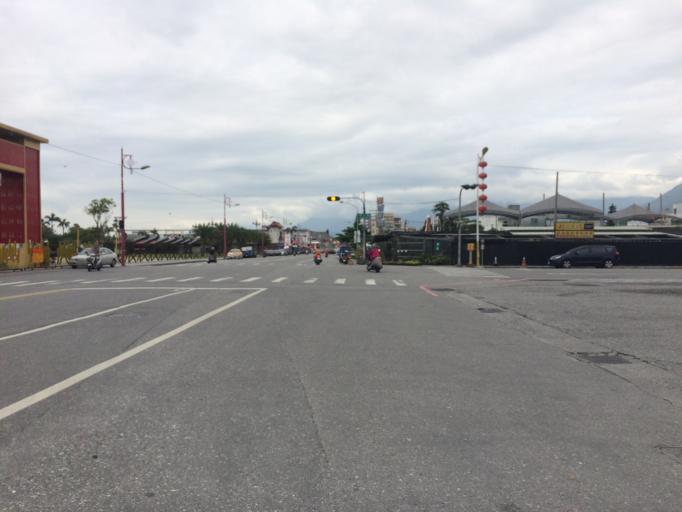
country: TW
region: Taiwan
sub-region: Hualien
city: Hualian
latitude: 23.9740
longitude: 121.6111
